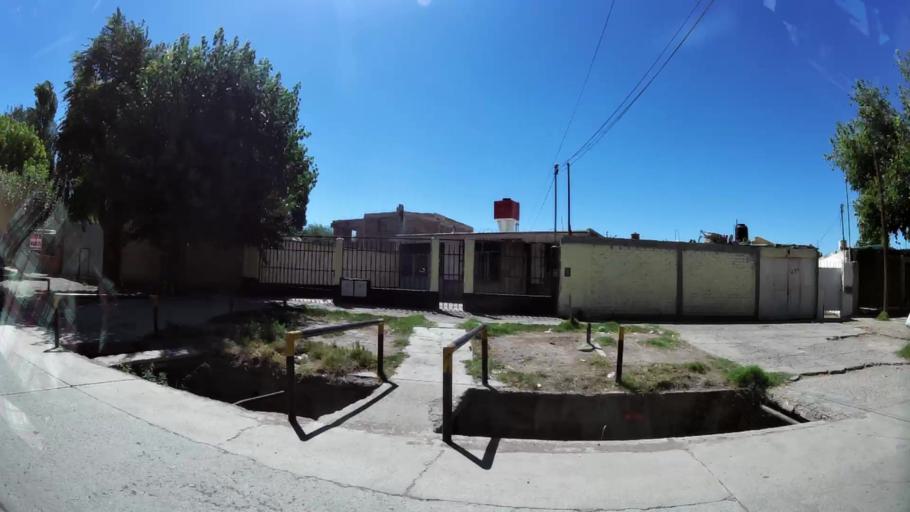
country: AR
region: Mendoza
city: Las Heras
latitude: -32.8318
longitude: -68.8360
